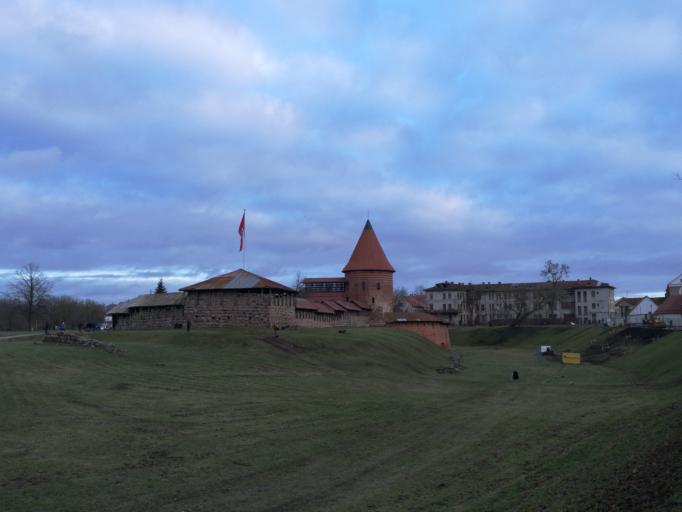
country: LT
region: Kauno apskritis
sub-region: Kaunas
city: Kaunas
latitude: 54.8988
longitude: 23.8826
